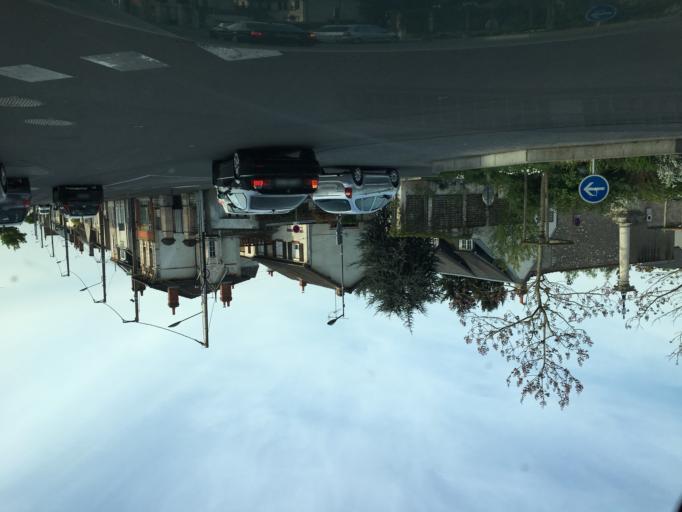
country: FR
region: Centre
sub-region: Departement du Loiret
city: Fleury-les-Aubrais
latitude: 47.9196
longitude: 1.9179
